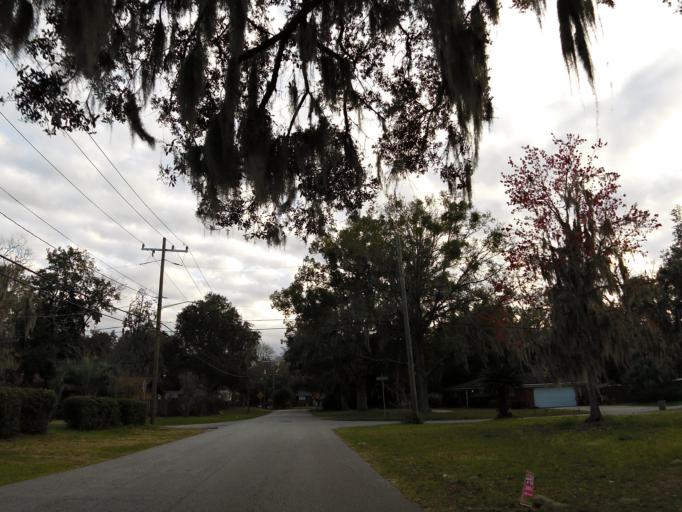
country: US
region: Florida
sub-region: Duval County
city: Jacksonville
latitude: 30.2933
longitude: -81.7262
